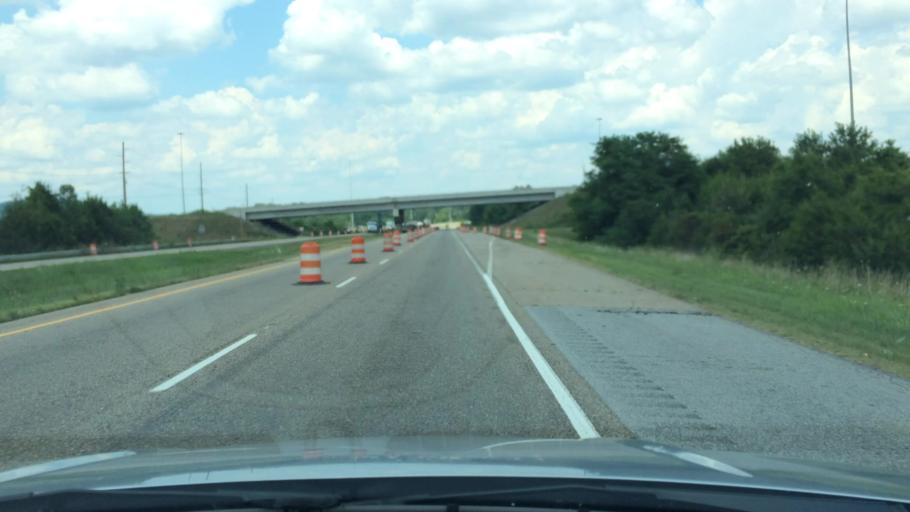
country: US
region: Tennessee
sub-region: Hamblen County
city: Morristown
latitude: 36.1739
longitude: -83.3482
